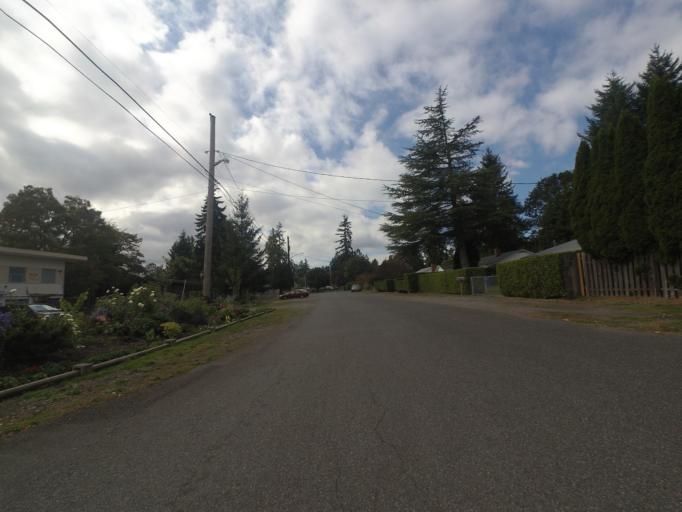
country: US
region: Washington
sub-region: Pierce County
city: Lakewood
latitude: 47.1707
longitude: -122.5237
